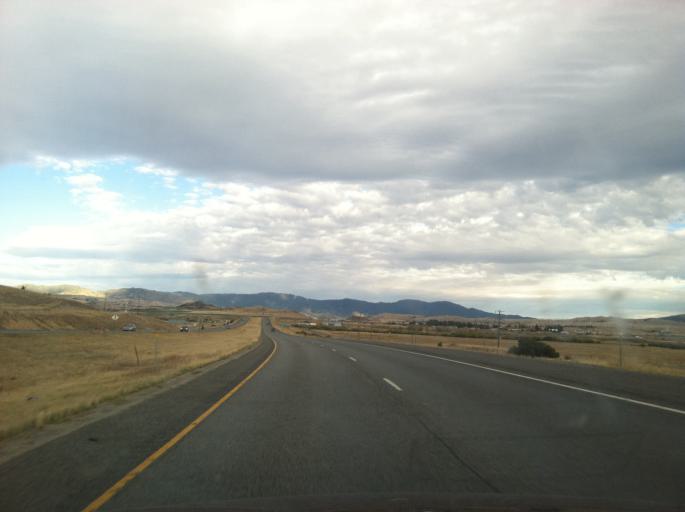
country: US
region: Montana
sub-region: Silver Bow County
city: Butte-Silver Bow (Balance)
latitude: 46.0100
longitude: -112.7060
